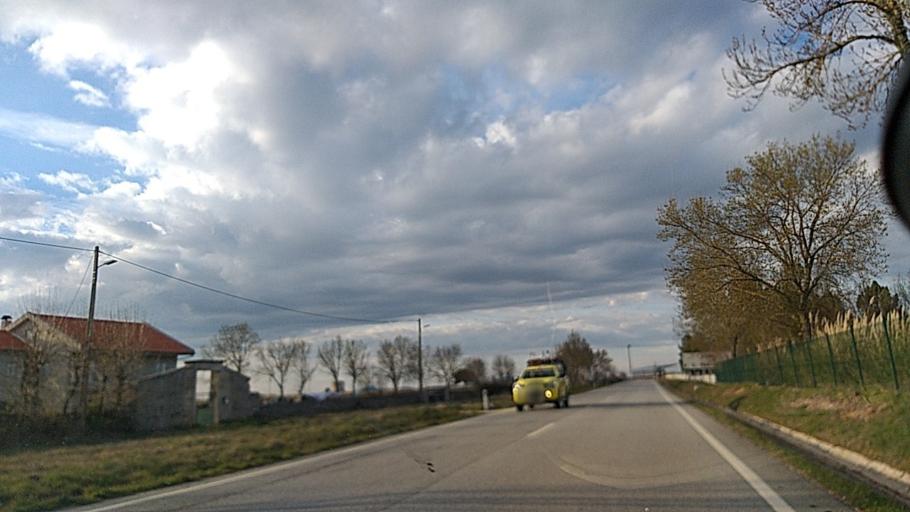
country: ES
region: Castille and Leon
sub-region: Provincia de Salamanca
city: Aldea del Obispo
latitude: 40.7089
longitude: -6.8973
